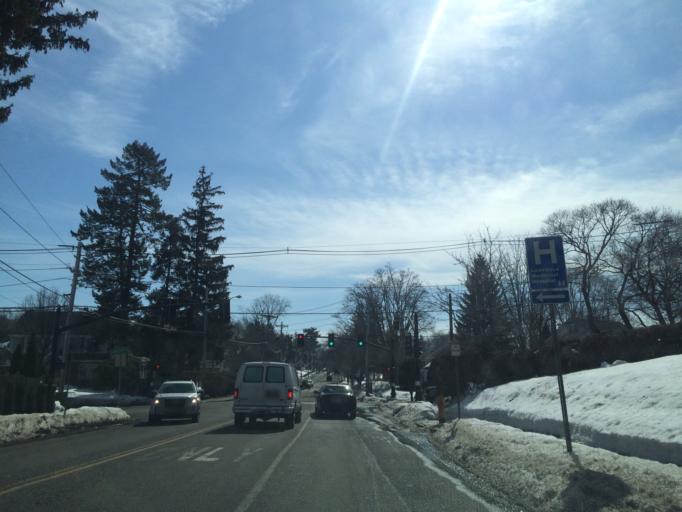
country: US
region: Massachusetts
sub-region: Middlesex County
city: Medford
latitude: 42.4242
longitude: -71.1215
